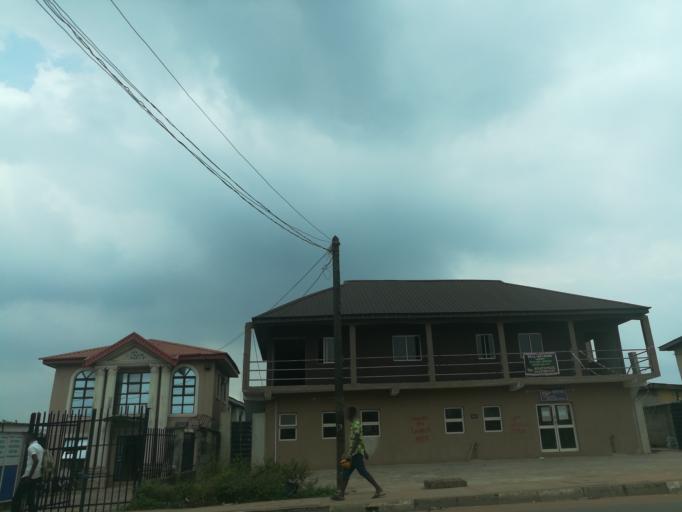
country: NG
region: Lagos
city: Ikorodu
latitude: 6.6182
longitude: 3.5161
